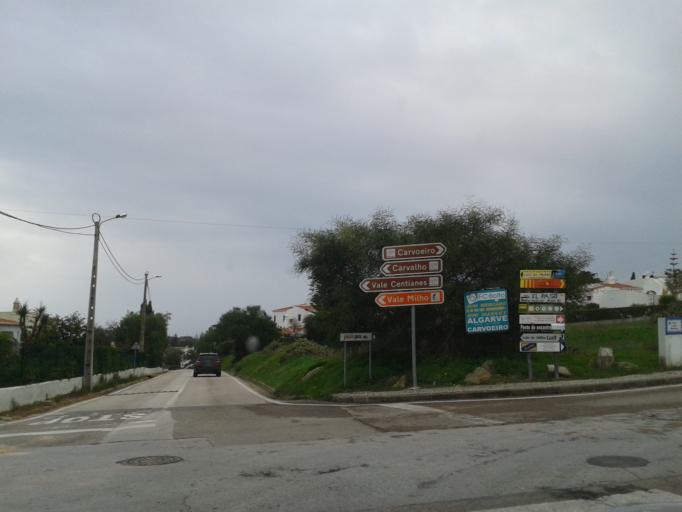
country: PT
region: Faro
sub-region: Lagoa
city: Carvoeiro
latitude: 37.1007
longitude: -8.4553
